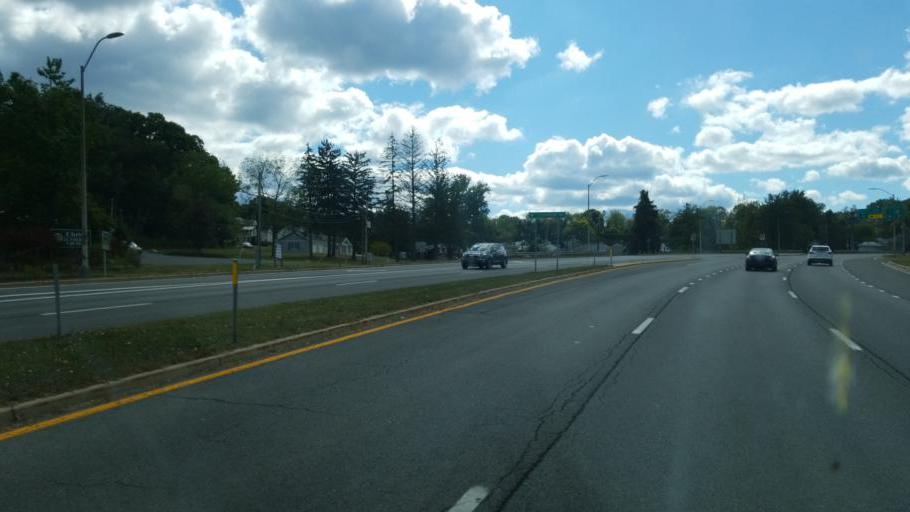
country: US
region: Maryland
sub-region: Allegany County
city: Bowling Green
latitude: 39.6341
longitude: -78.8302
